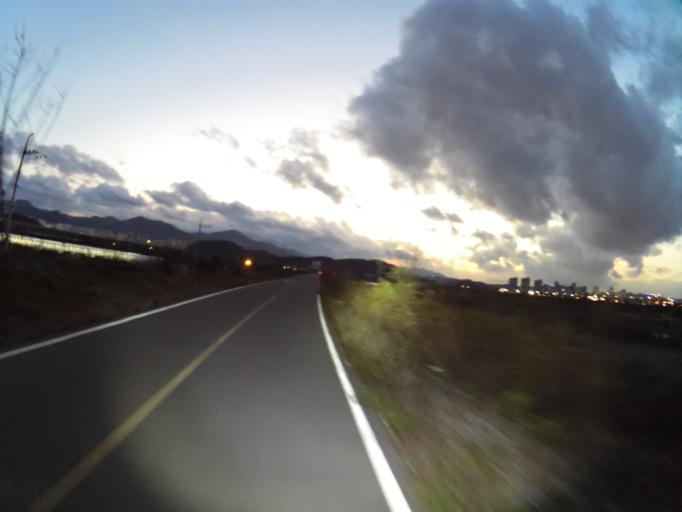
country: KR
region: Gyeongsangbuk-do
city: Gyeongsan-si
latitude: 35.8604
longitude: 128.7142
